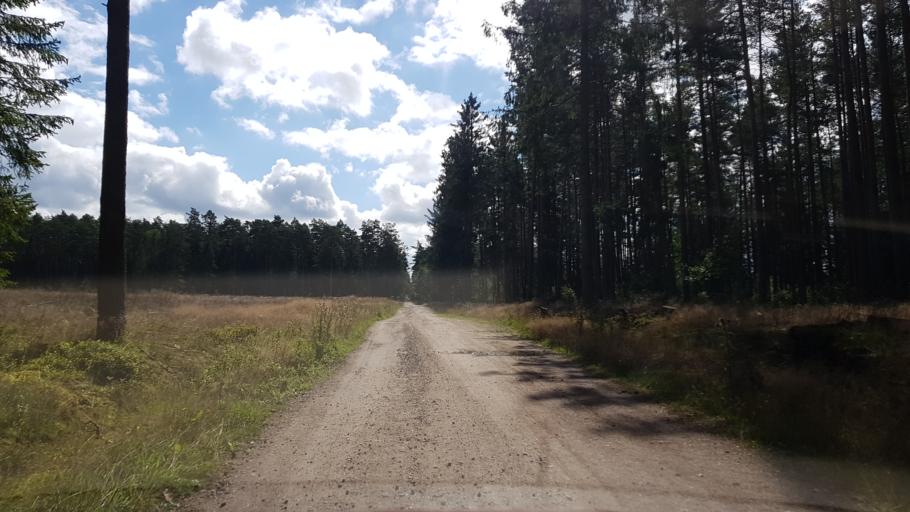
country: PL
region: West Pomeranian Voivodeship
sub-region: Powiat bialogardzki
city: Tychowo
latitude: 54.0209
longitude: 16.2985
